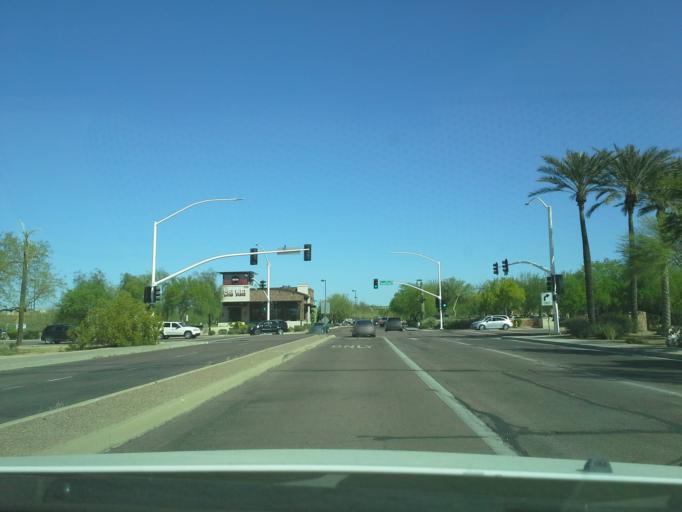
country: US
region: Arizona
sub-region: Maricopa County
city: Paradise Valley
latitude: 33.6176
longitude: -111.8932
